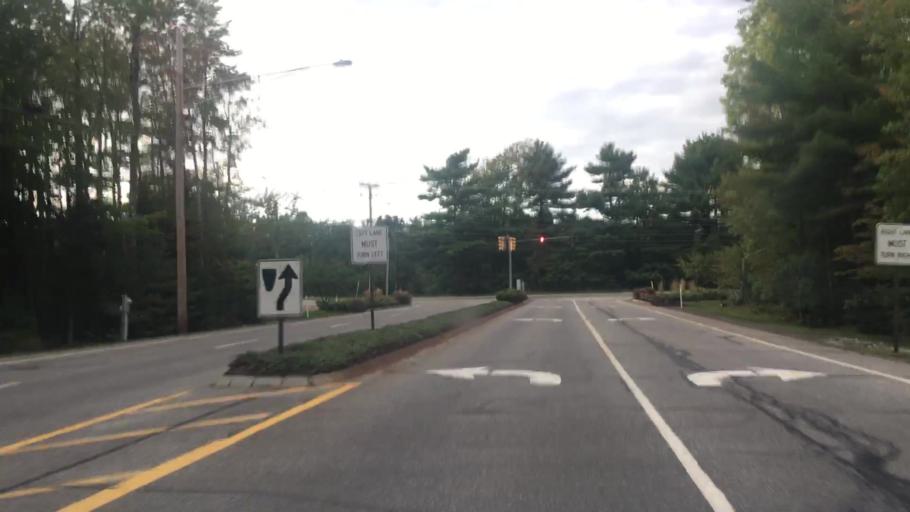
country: US
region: Maine
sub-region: Cumberland County
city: Brunswick
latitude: 43.9109
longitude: -69.8978
